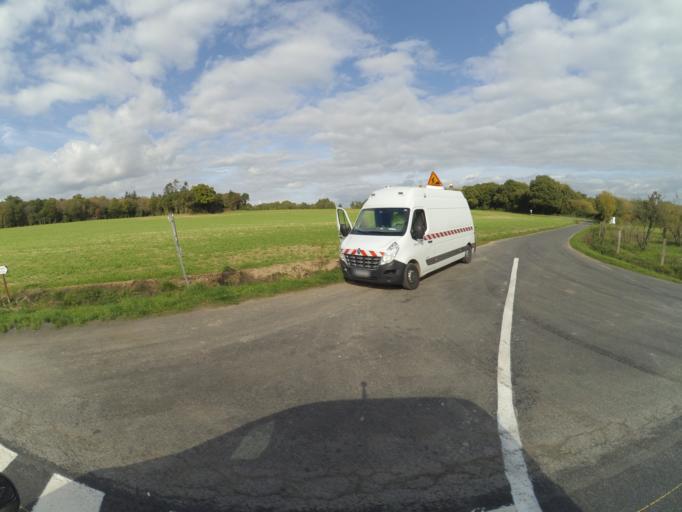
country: FR
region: Pays de la Loire
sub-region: Departement de la Loire-Atlantique
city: Fegreac
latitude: 47.6008
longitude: -2.0198
